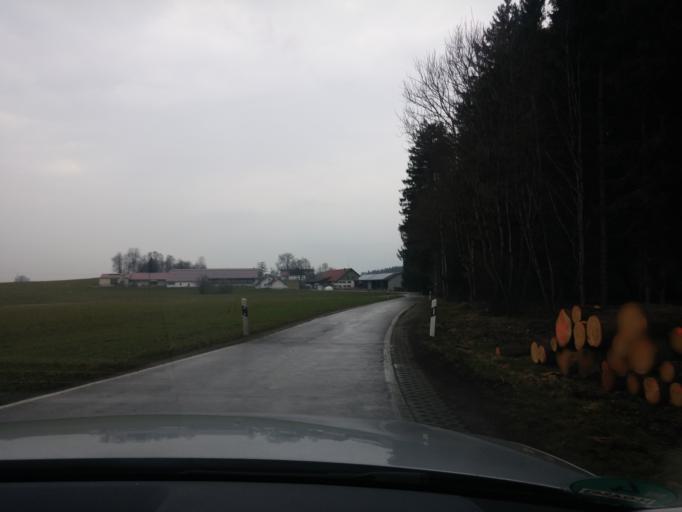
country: DE
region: Baden-Wuerttemberg
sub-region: Tuebingen Region
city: Aichstetten
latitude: 47.8481
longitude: 10.0823
